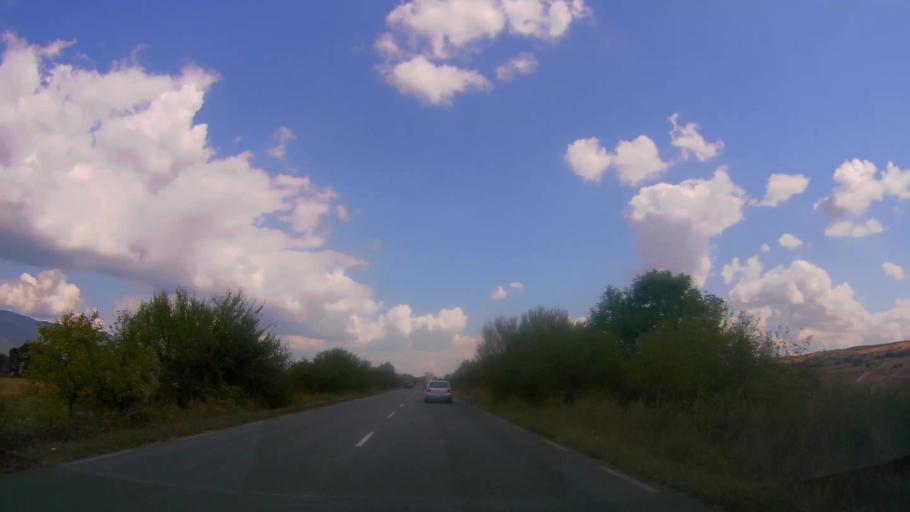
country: BG
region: Sliven
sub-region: Obshtina Tvurditsa
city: Tvurditsa
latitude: 42.6572
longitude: 25.9109
